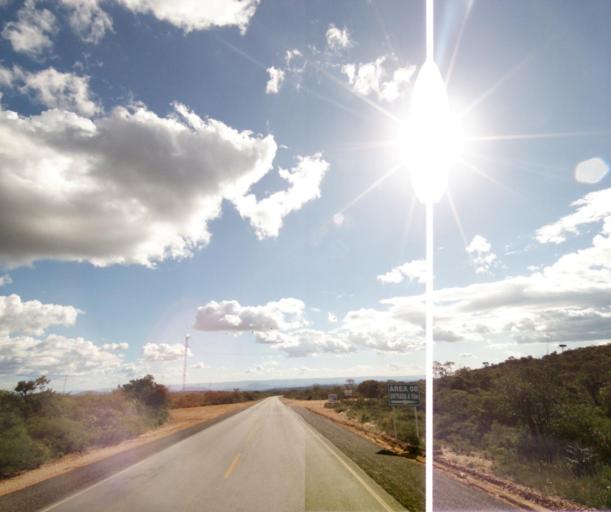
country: BR
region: Bahia
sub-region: Caetite
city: Caetite
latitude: -14.1204
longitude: -42.6103
